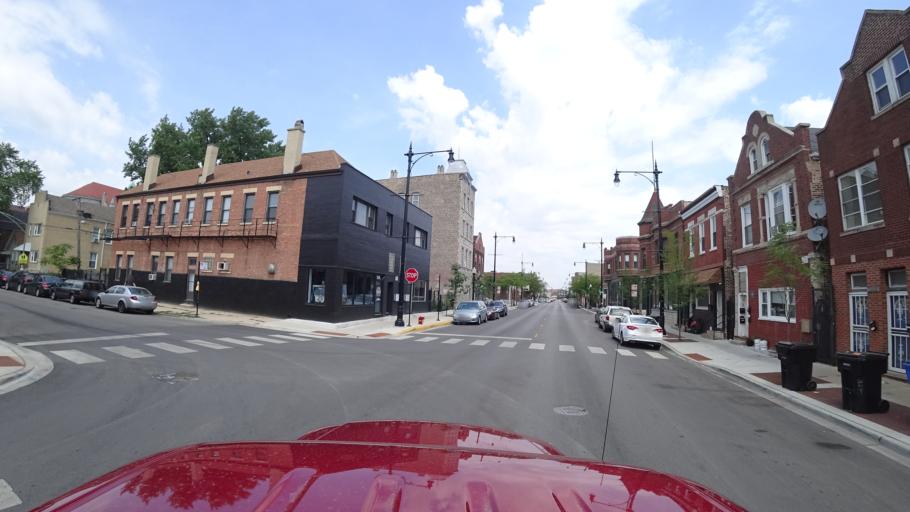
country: US
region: Illinois
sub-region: Cook County
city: Chicago
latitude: 41.8352
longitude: -87.6511
